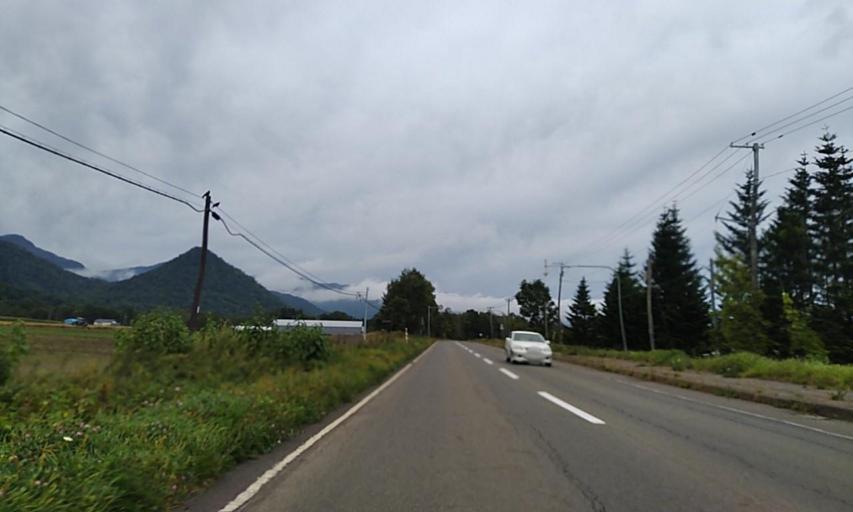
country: JP
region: Hokkaido
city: Bihoro
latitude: 43.5618
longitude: 144.3153
